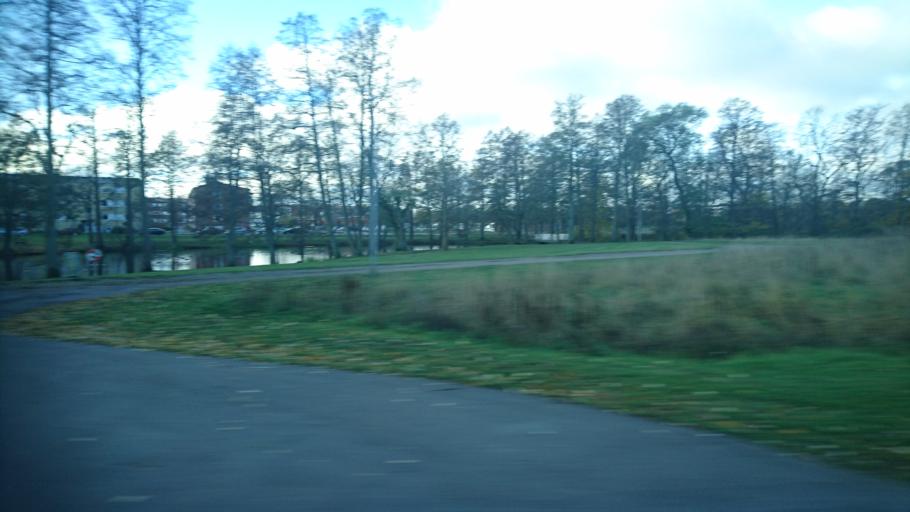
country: SE
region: Vaestmanland
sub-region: Sala Kommun
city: Sala
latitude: 59.9260
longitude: 16.5957
